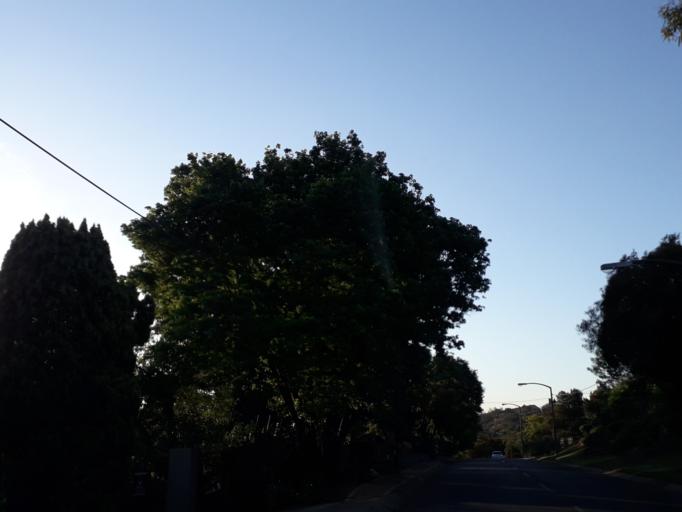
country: ZA
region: Gauteng
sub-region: City of Johannesburg Metropolitan Municipality
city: Roodepoort
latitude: -26.1600
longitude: 27.9369
